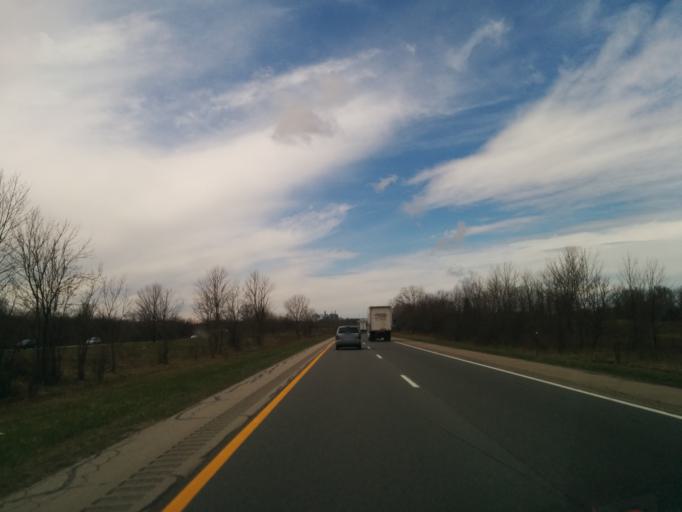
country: US
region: Michigan
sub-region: Ottawa County
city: Zeeland
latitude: 42.8187
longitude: -85.9532
